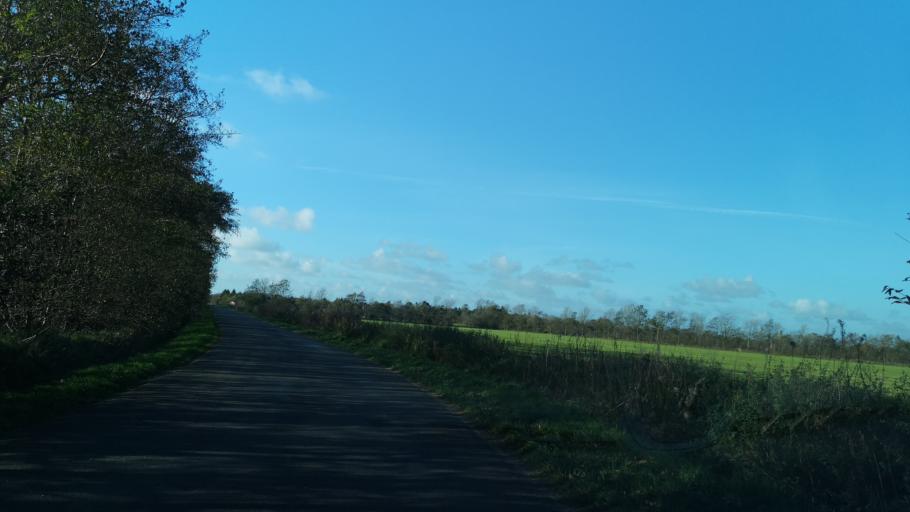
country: DK
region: Central Jutland
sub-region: Ringkobing-Skjern Kommune
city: Tarm
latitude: 55.8247
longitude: 8.4013
